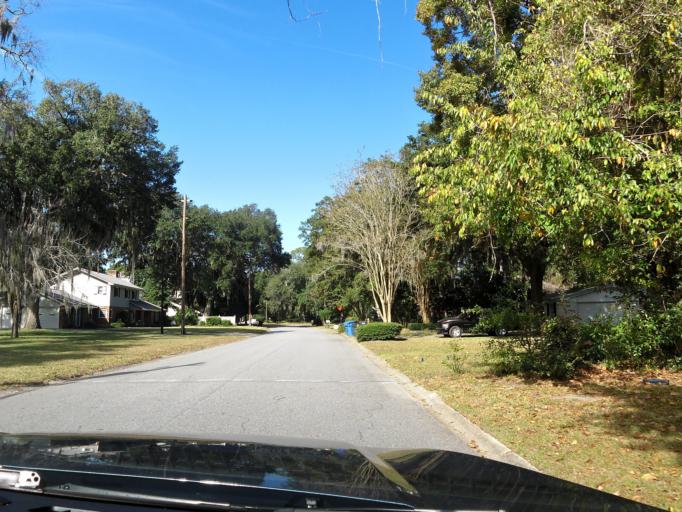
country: US
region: Georgia
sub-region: Glynn County
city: Brunswick
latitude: 31.1289
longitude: -81.5582
